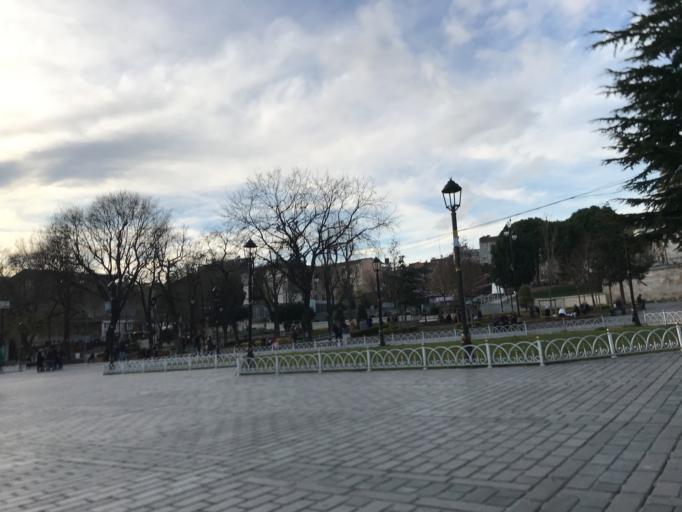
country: TR
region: Istanbul
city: Eminoenue
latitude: 41.0074
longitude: 28.9769
